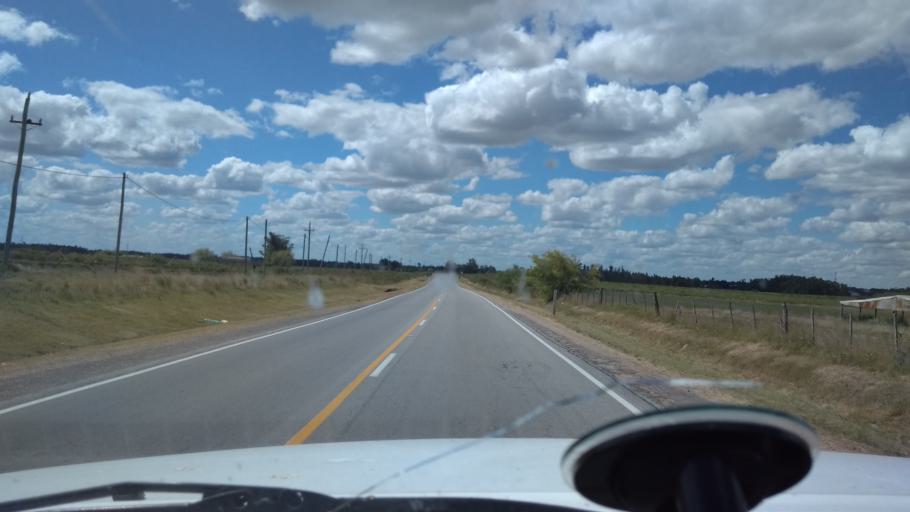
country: UY
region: Canelones
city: Santa Rosa
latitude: -34.5213
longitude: -56.0544
